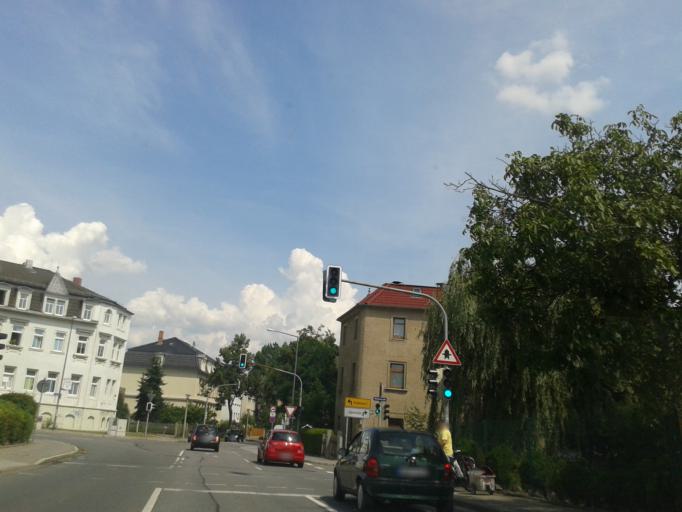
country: DE
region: Saxony
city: Radebeul
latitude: 51.0876
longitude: 13.6982
